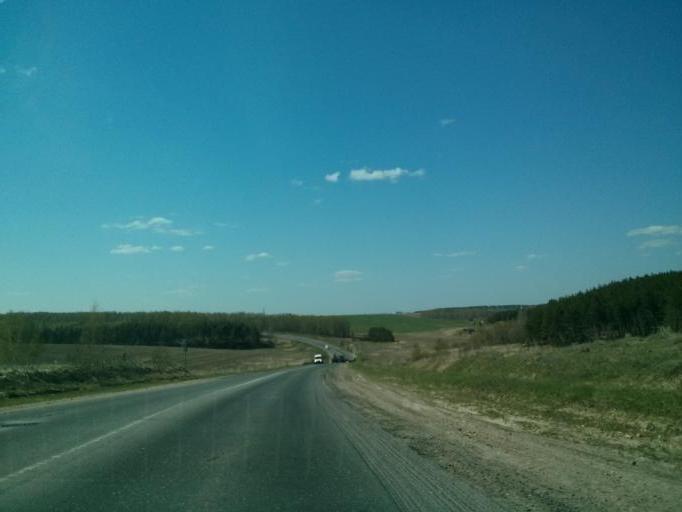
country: RU
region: Nizjnij Novgorod
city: Vorsma
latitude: 55.9608
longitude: 43.1916
